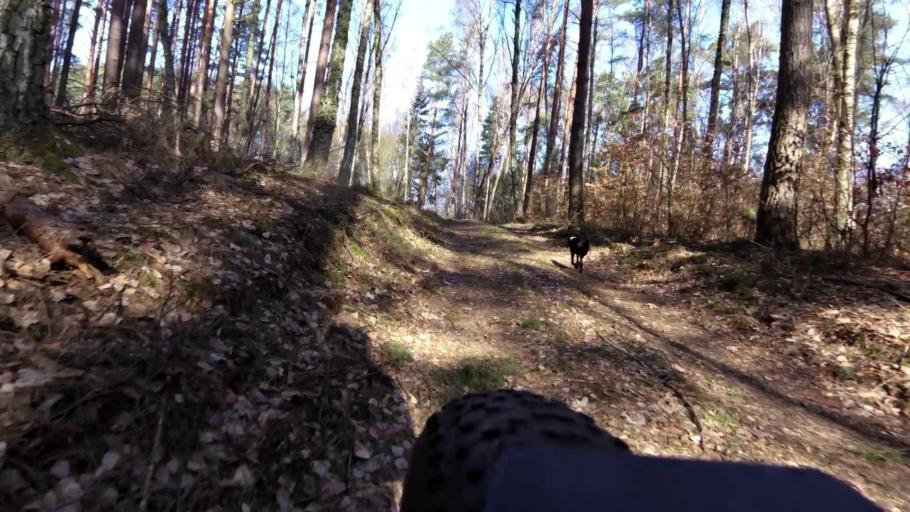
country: PL
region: Lubusz
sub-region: Powiat sulecinski
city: Torzym
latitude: 52.2198
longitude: 14.9693
